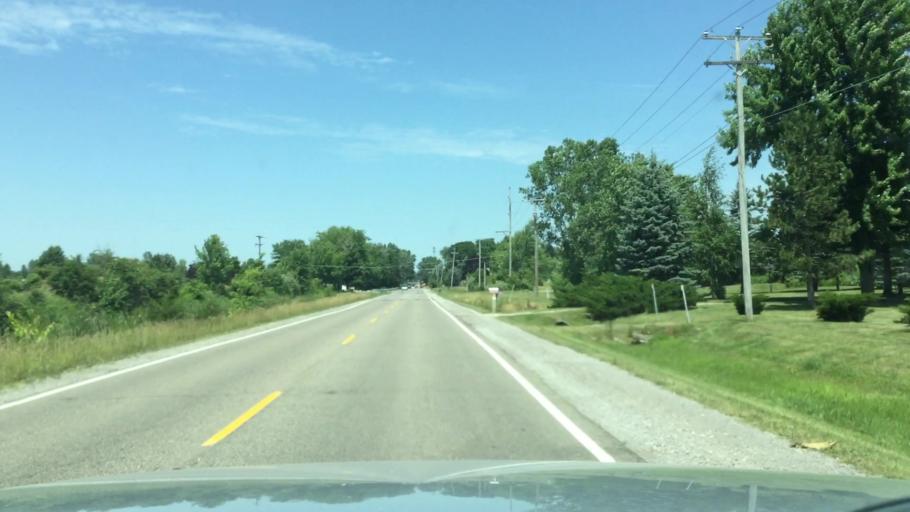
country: US
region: Michigan
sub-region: Genesee County
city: Swartz Creek
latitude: 42.9523
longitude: -83.8110
